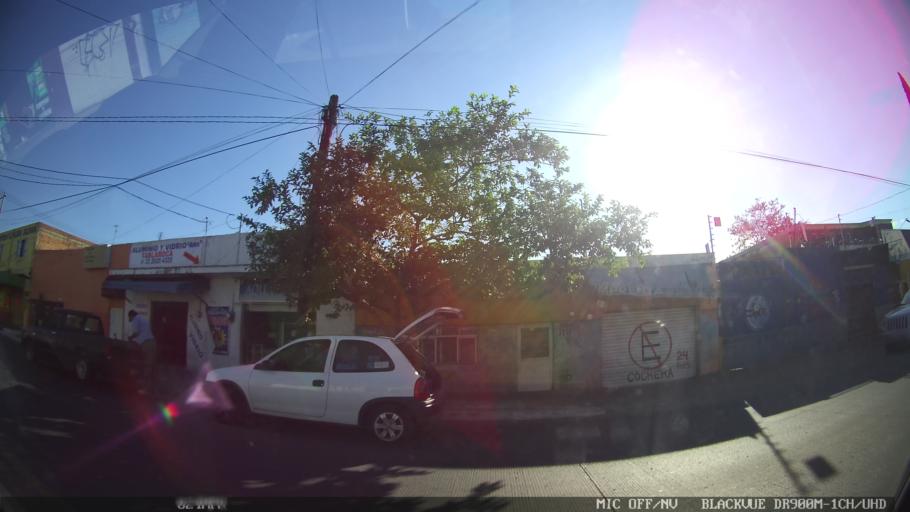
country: MX
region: Jalisco
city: Tlaquepaque
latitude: 20.7094
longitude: -103.2964
